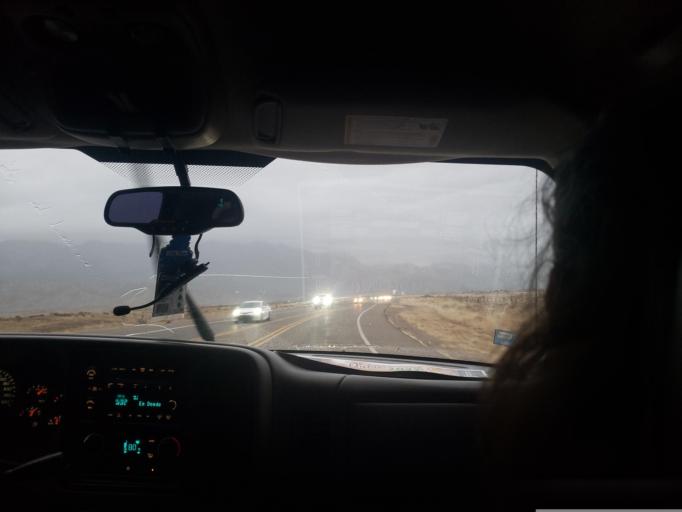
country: US
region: New Mexico
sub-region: Sandoval County
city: Corrales
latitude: 35.2024
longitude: -106.5557
